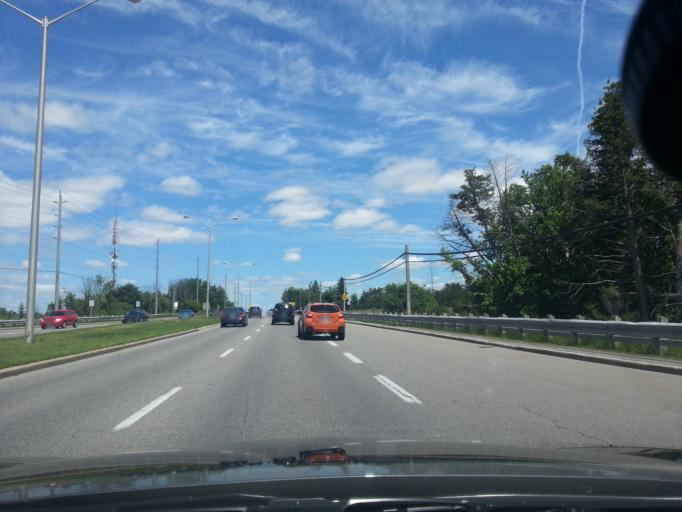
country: CA
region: Ontario
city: Bells Corners
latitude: 45.3046
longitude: -75.8752
